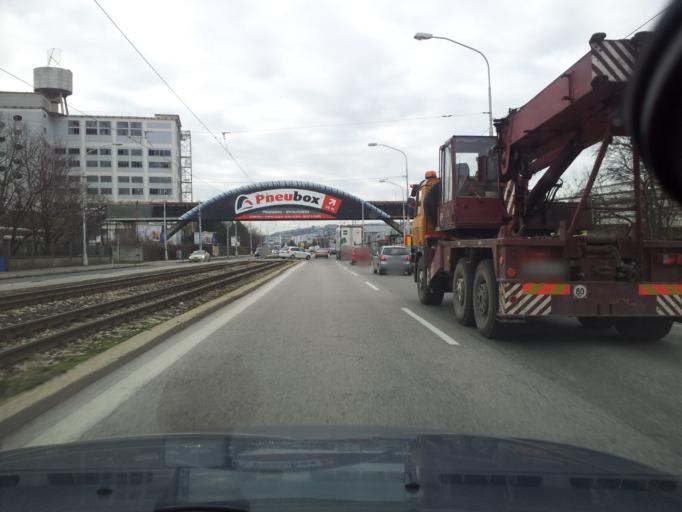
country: SK
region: Bratislavsky
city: Bratislava
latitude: 48.1788
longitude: 17.1510
